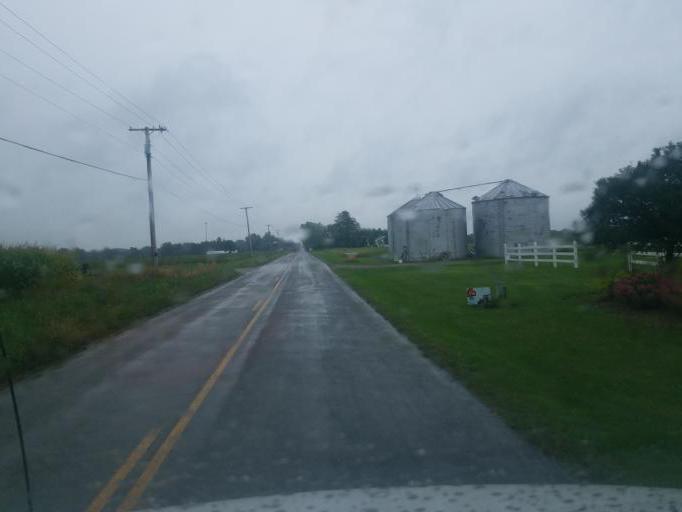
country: US
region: Ohio
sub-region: Medina County
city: Seville
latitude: 41.0413
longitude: -81.8323
